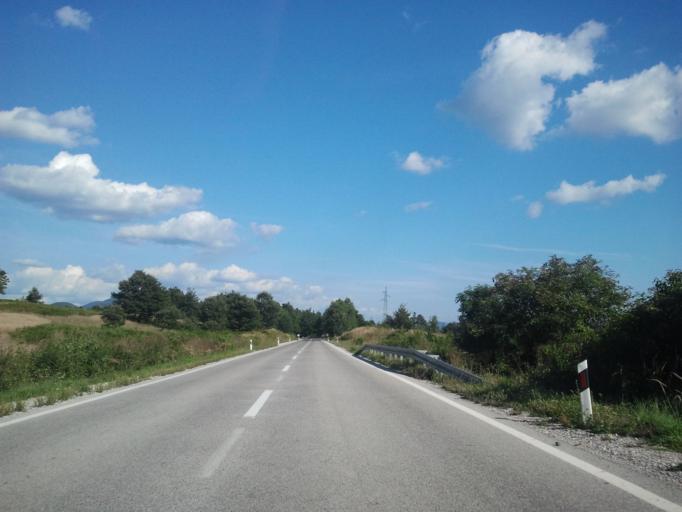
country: HR
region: Zadarska
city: Obrovac
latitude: 44.3786
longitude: 15.6476
